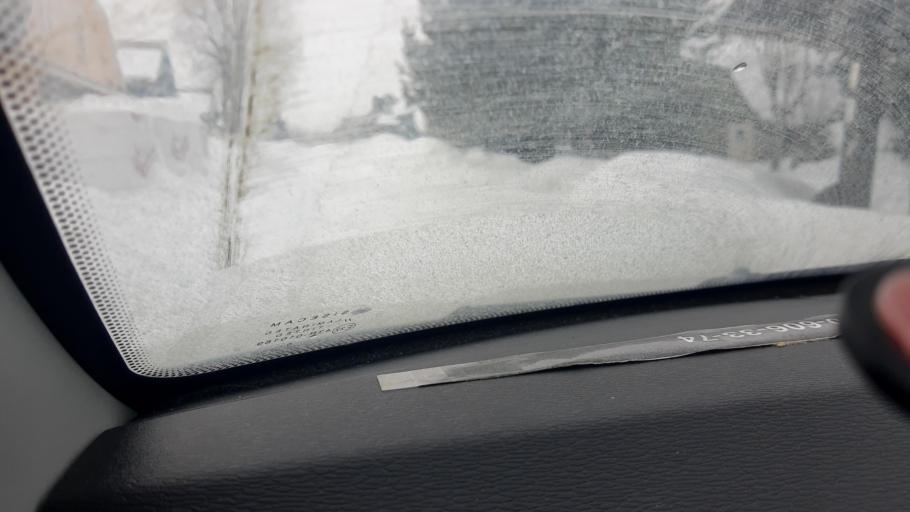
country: RU
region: Nizjnij Novgorod
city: Sitniki
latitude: 56.5310
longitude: 44.0636
